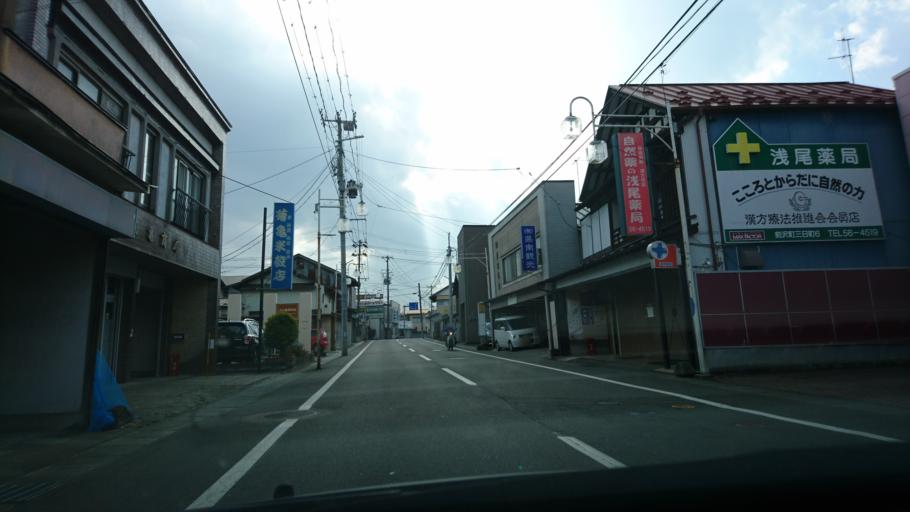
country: JP
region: Iwate
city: Mizusawa
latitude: 39.0473
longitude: 141.1225
